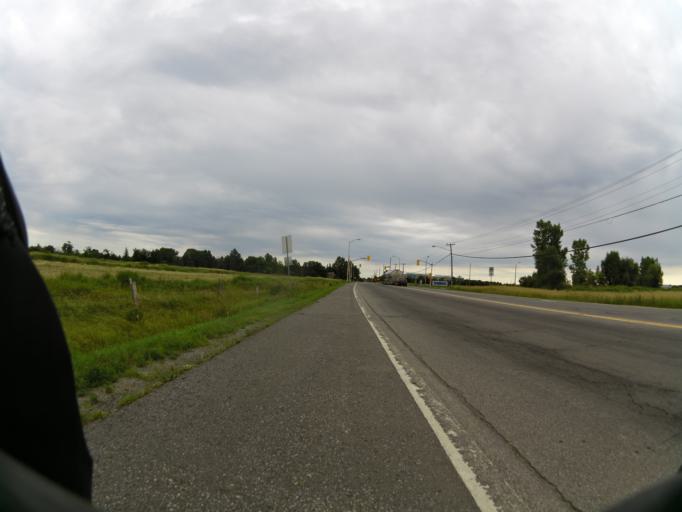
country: CA
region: Ontario
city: Ottawa
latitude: 45.3024
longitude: -75.7056
